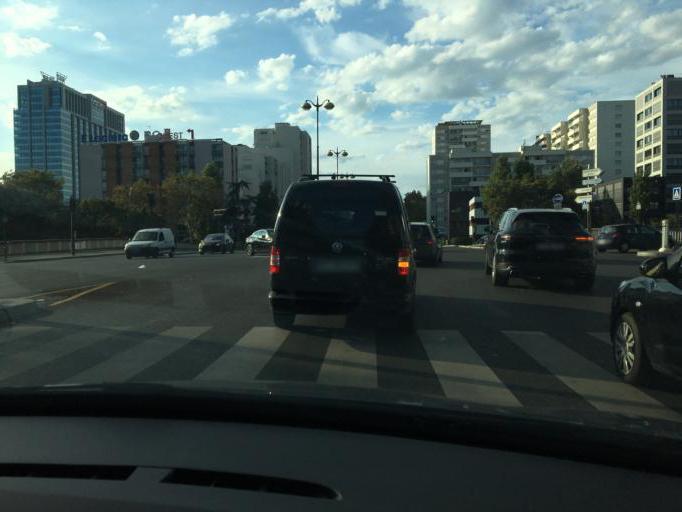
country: FR
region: Ile-de-France
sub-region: Departement des Hauts-de-Seine
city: Clichy
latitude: 48.8916
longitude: 2.3019
